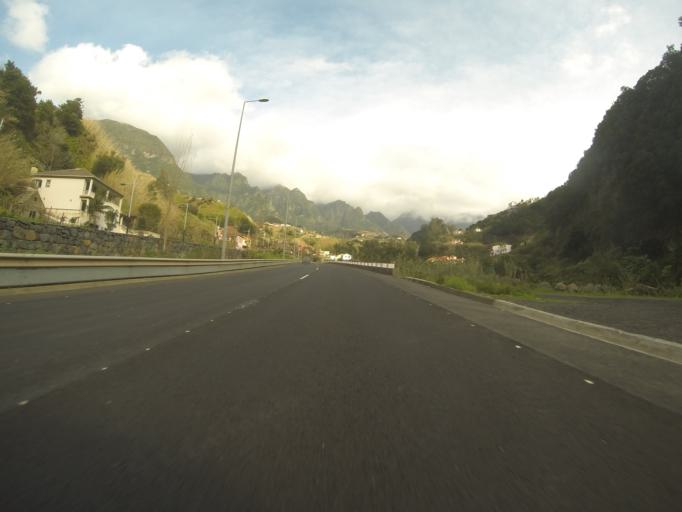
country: PT
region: Madeira
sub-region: Sao Vicente
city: Sao Vicente
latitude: 32.7931
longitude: -17.0360
